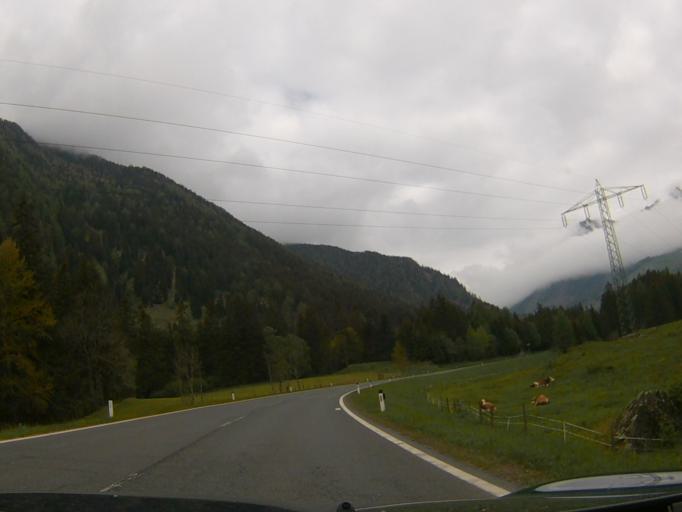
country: AT
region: Carinthia
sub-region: Politischer Bezirk Spittal an der Drau
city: Obervellach
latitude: 46.9473
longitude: 13.1825
